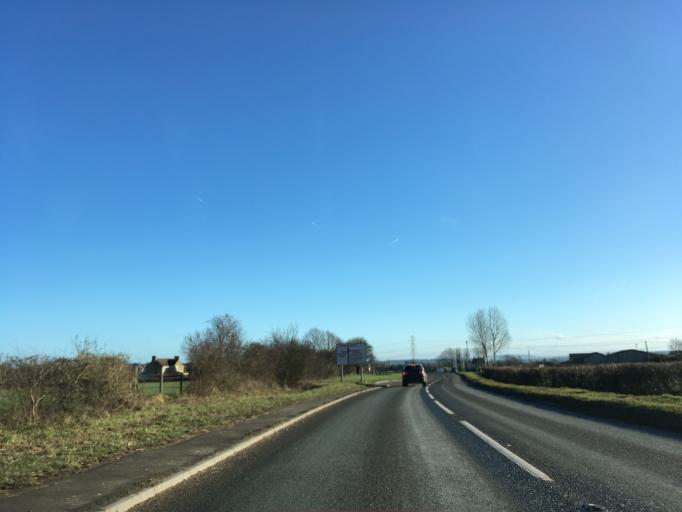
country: GB
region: England
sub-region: Wiltshire
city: Chippenham
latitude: 51.4704
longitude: -2.1538
